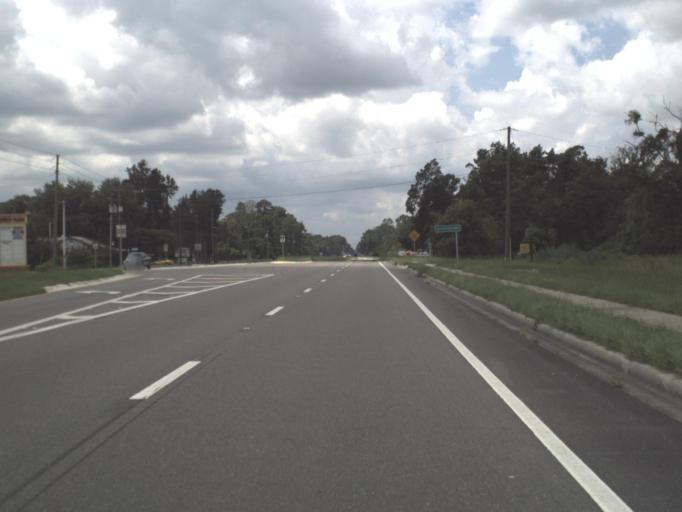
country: US
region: Florida
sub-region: Hernando County
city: Masaryktown
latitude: 28.4526
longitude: -82.4517
